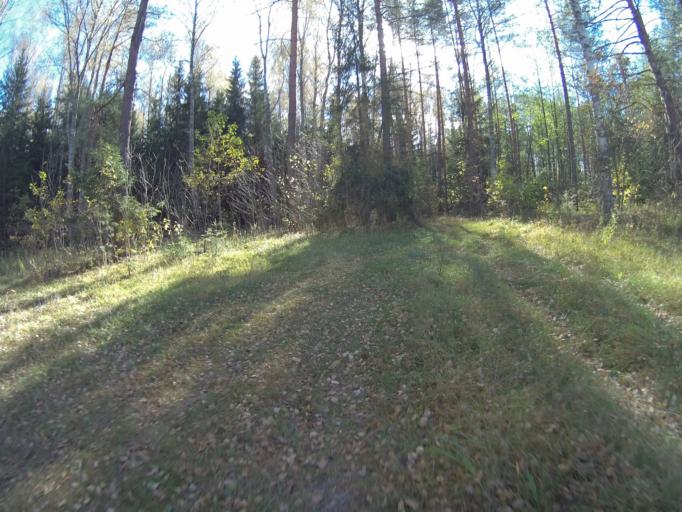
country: RU
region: Vladimir
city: Golovino
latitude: 56.0123
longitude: 40.4856
